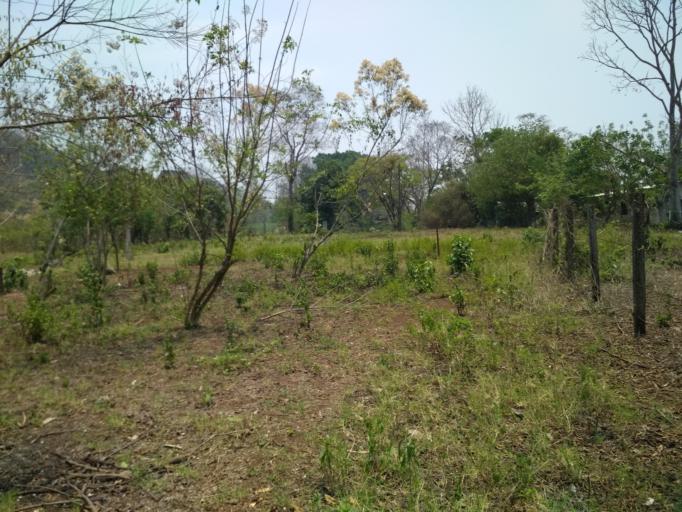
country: MX
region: Veracruz
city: Cosolapa
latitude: 18.5908
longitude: -96.6972
